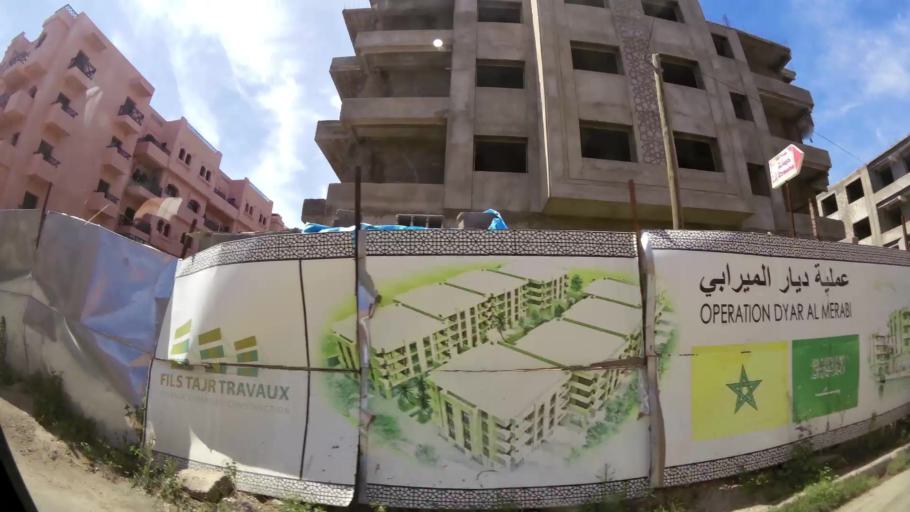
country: MA
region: Marrakech-Tensift-Al Haouz
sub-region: Marrakech
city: Marrakesh
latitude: 31.6619
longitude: -7.9877
